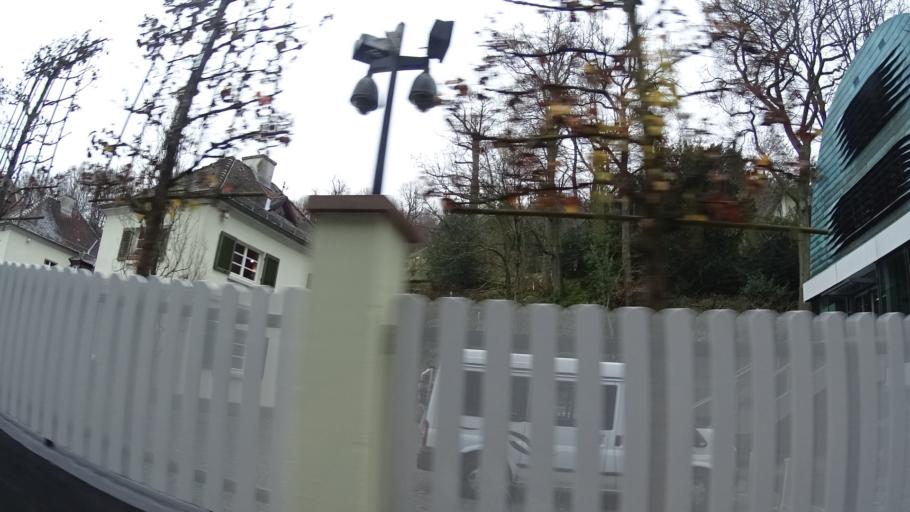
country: DE
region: Baden-Wuerttemberg
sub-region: Karlsruhe Region
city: Heidelberg
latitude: 49.4157
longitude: 8.7298
